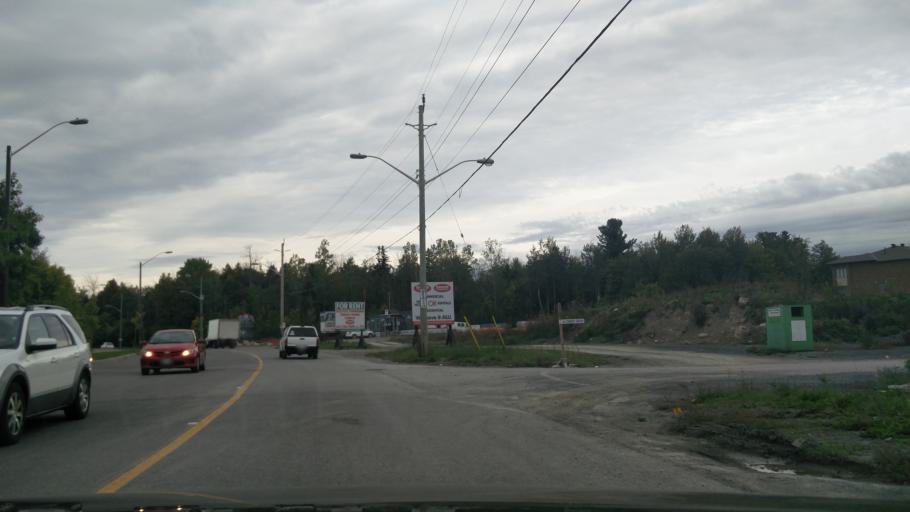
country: CA
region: Ontario
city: Bells Corners
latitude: 45.2833
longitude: -75.7450
